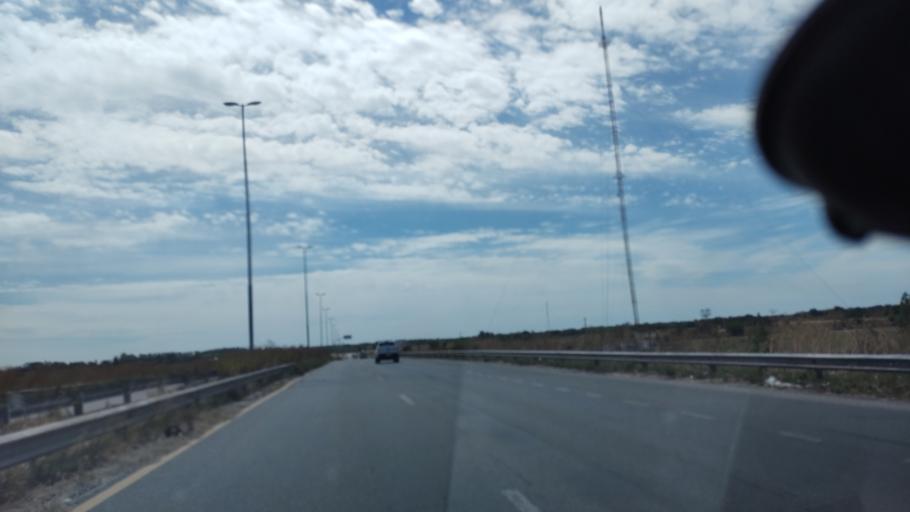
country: AR
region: Buenos Aires
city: Canuelas
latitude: -35.0277
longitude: -58.7316
